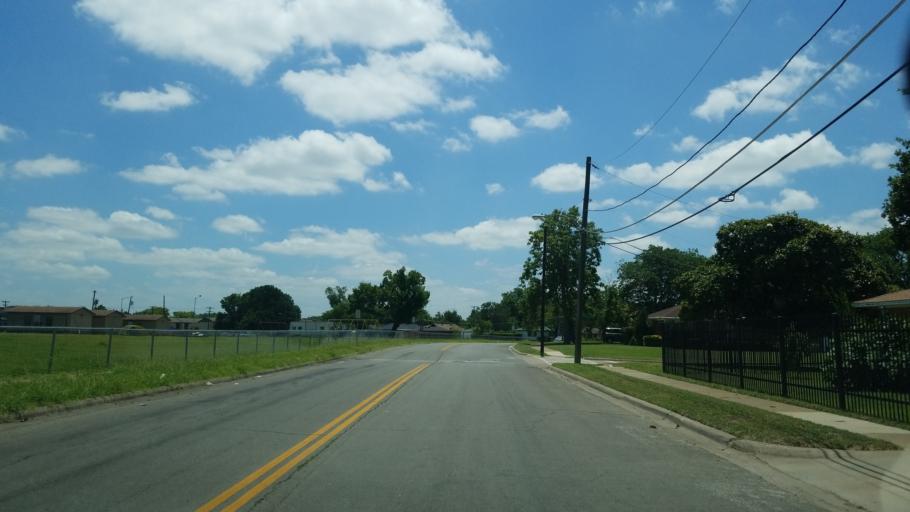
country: US
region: Texas
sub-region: Dallas County
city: Balch Springs
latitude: 32.7406
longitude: -96.7026
